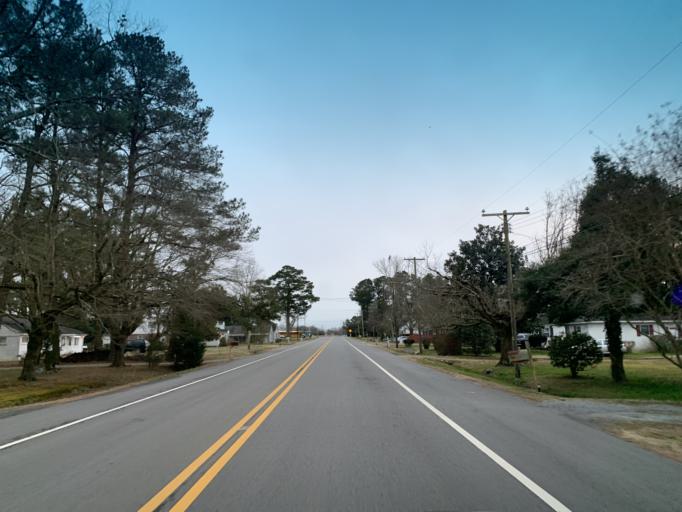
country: US
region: Maryland
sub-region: Worcester County
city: Pocomoke City
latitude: 38.0703
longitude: -75.5469
